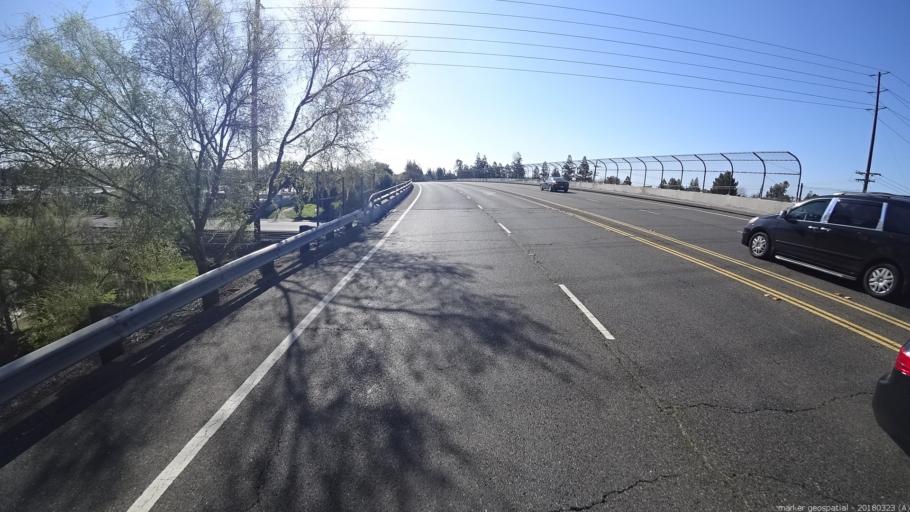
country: US
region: California
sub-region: Sacramento County
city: North Highlands
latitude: 38.6785
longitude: -121.3630
